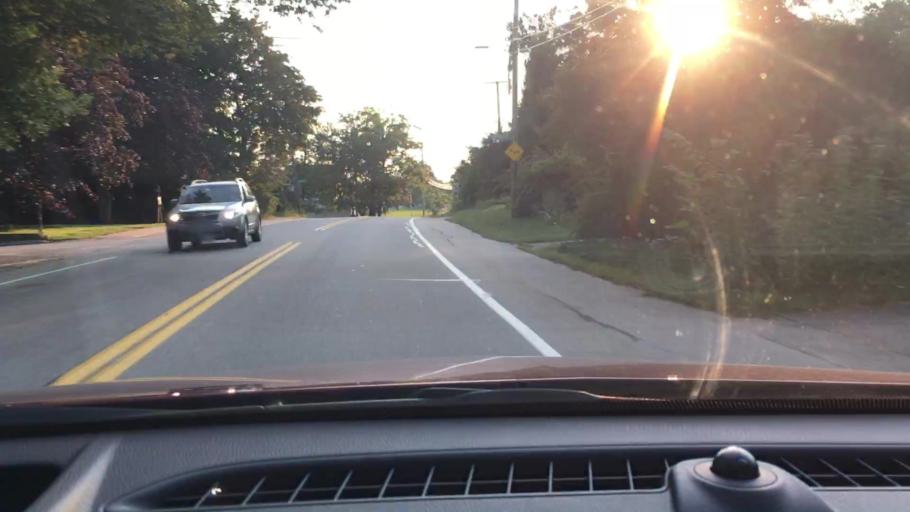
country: US
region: New Hampshire
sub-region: Rockingham County
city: Portsmouth
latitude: 43.0582
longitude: -70.7809
